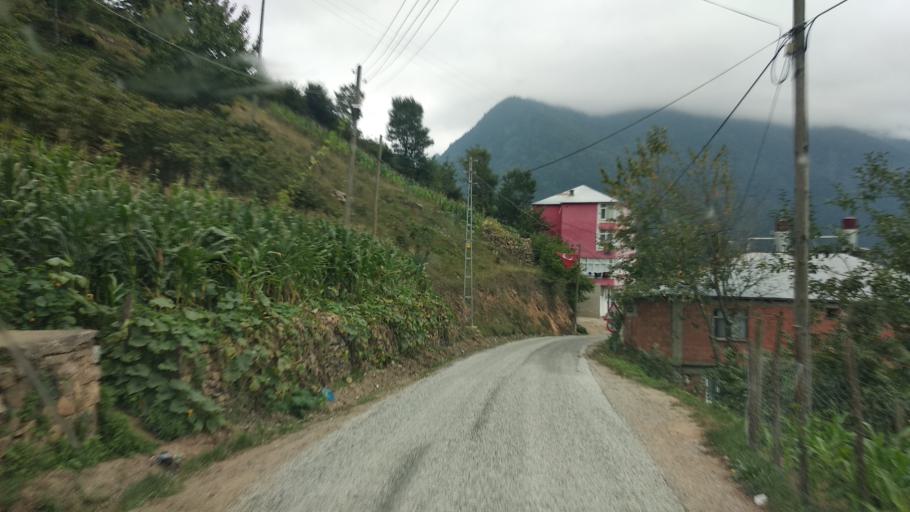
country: TR
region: Giresun
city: Dogankent
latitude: 40.7446
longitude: 38.9911
